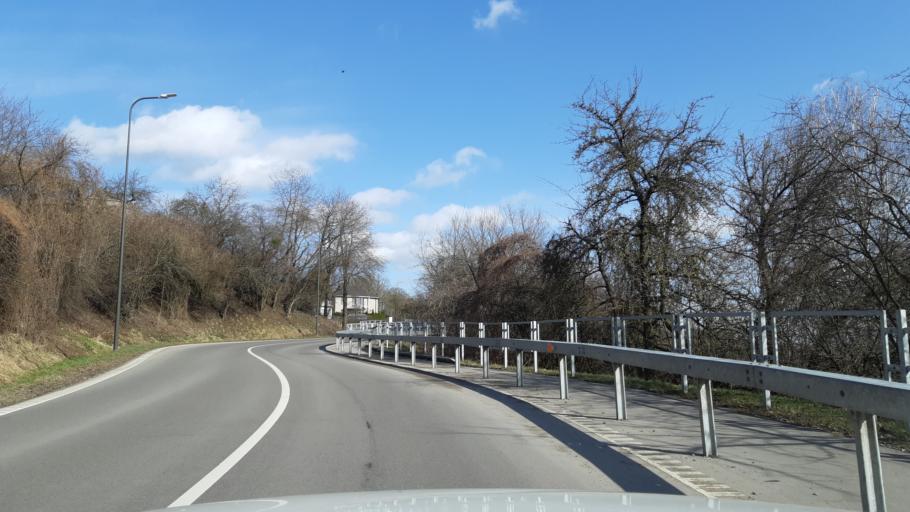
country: LT
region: Kauno apskritis
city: Dainava (Kaunas)
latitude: 54.8925
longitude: 23.9584
